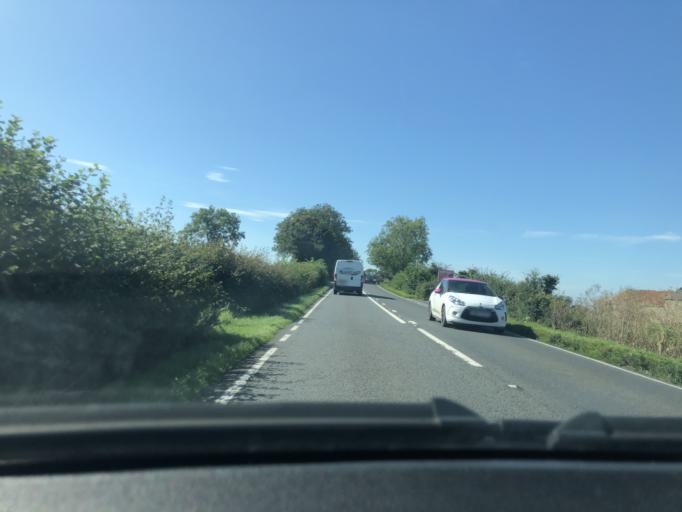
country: GB
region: England
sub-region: Somerset
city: Westonzoyland
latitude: 51.1405
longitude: -2.8739
